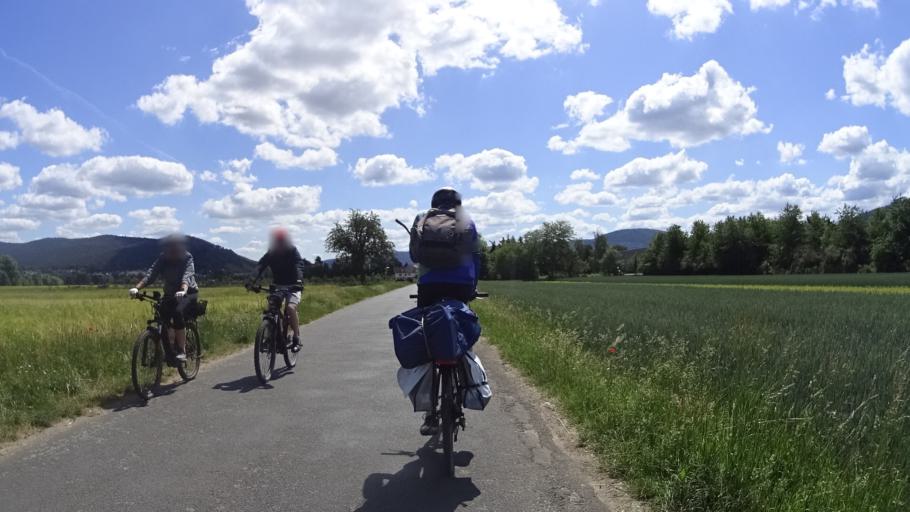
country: DE
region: Bavaria
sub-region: Regierungsbezirk Unterfranken
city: Kleinheubach
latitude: 49.7272
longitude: 9.2018
